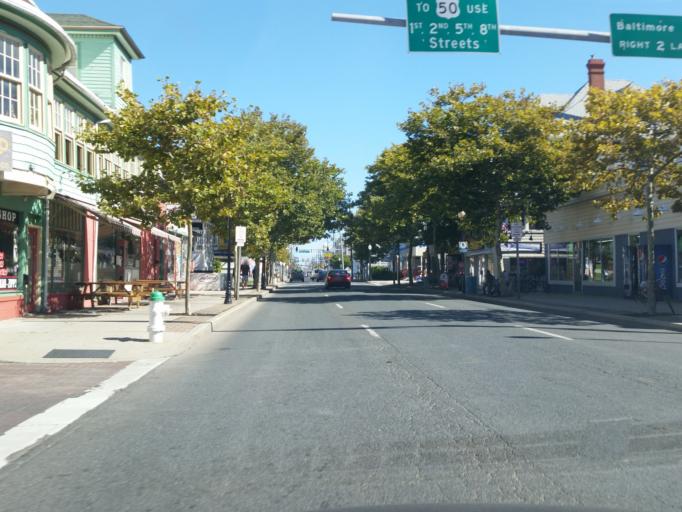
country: US
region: Maryland
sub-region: Worcester County
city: Ocean City
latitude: 38.3304
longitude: -75.0867
